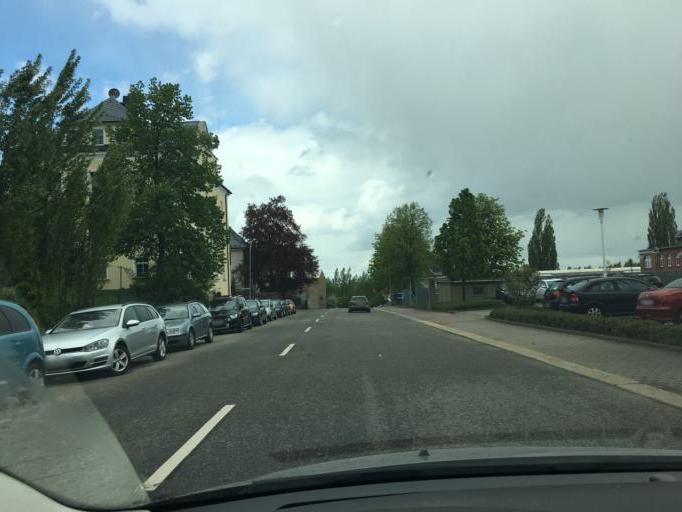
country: DE
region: Saxony
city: Limbach-Oberfrohna
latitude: 50.8586
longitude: 12.7758
